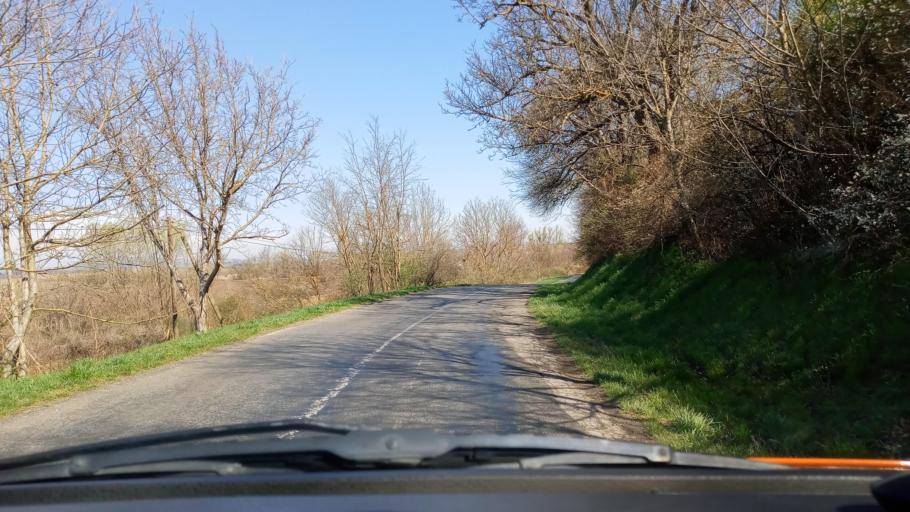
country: HU
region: Baranya
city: Boly
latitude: 46.0185
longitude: 18.4557
